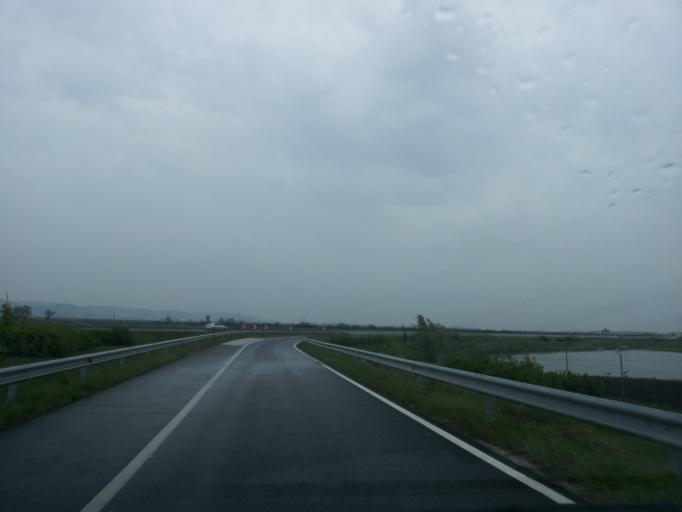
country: HU
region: Tolna
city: Ocseny
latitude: 46.3095
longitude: 18.7273
